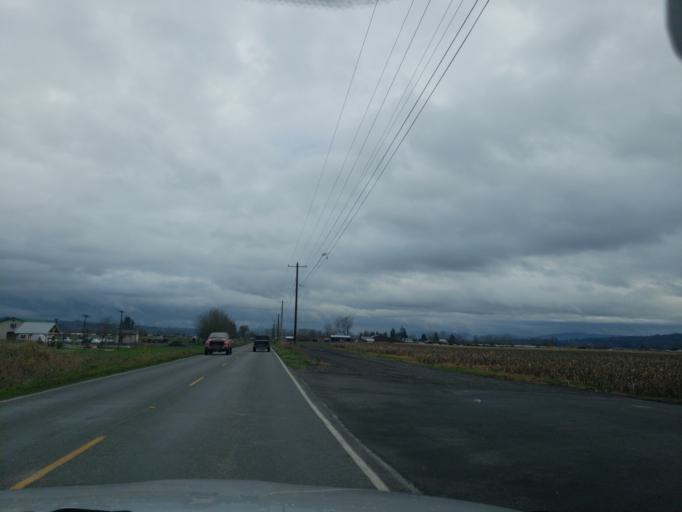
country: US
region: Washington
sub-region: Snohomish County
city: Snohomish
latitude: 47.8990
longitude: -122.1201
